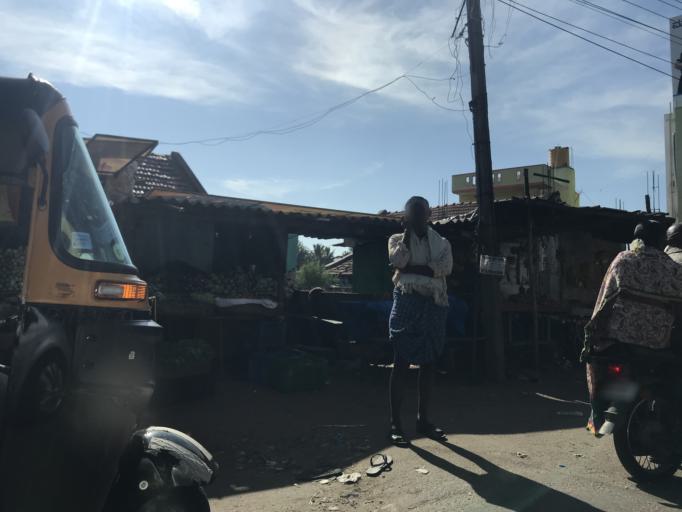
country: IN
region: Karnataka
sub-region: Mysore
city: Mysore
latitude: 12.2531
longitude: 76.6197
